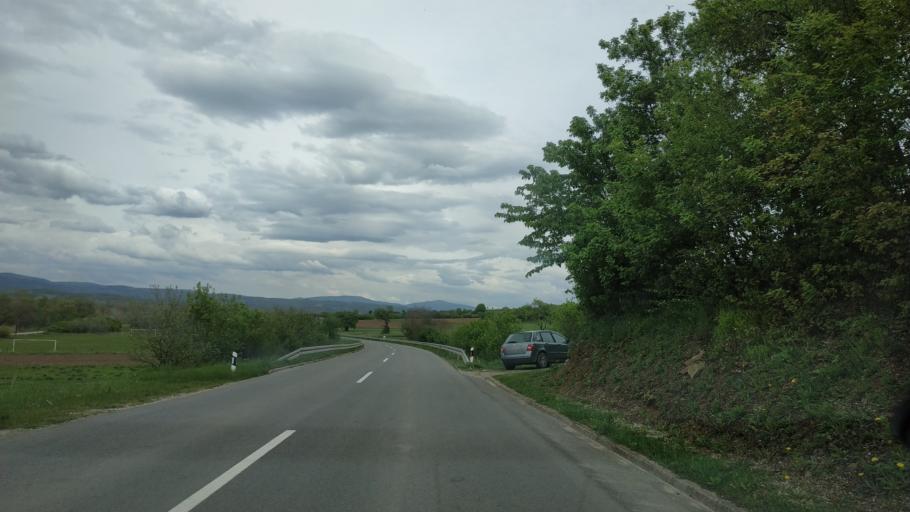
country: RS
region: Central Serbia
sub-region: Zajecarski Okrug
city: Soko Banja
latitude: 43.6520
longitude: 21.7633
